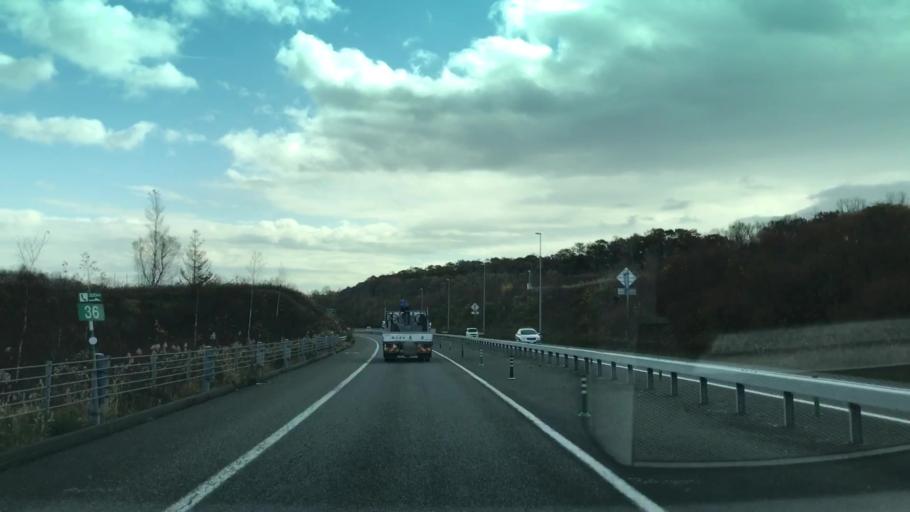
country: JP
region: Hokkaido
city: Tomakomai
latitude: 42.5457
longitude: 141.9982
